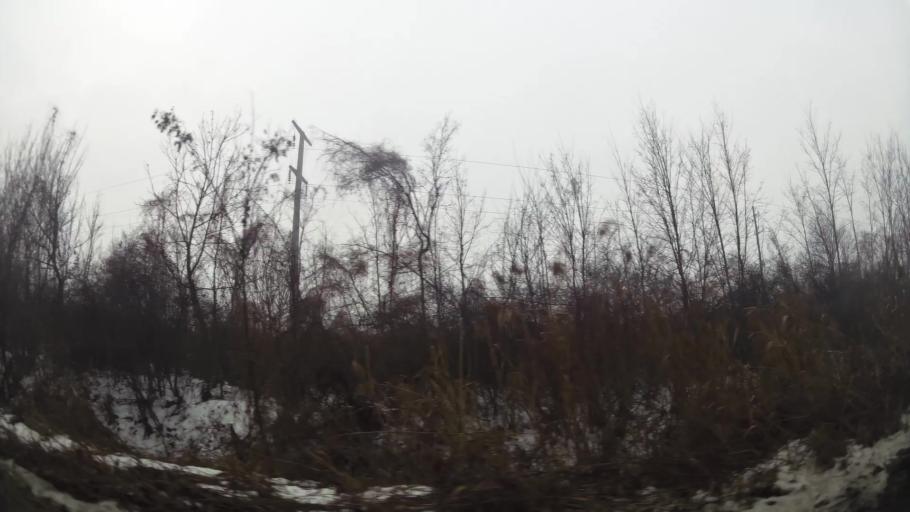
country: MK
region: Ilinden
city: Idrizovo
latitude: 41.9501
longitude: 21.5870
